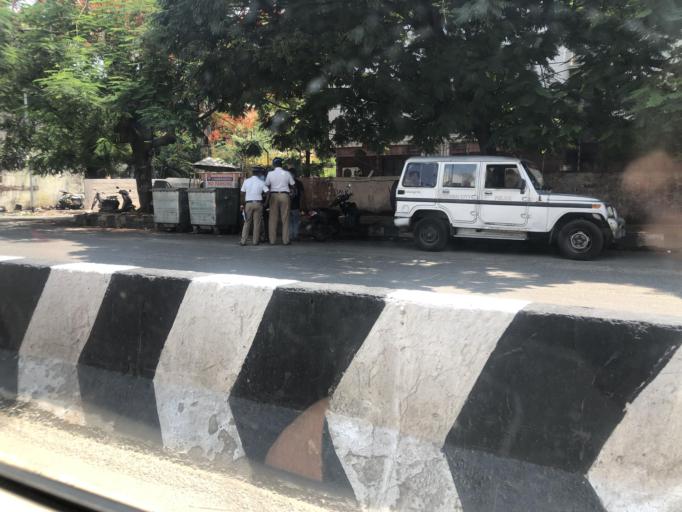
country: IN
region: Tamil Nadu
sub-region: Chennai
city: Gandhi Nagar
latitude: 12.9838
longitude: 80.2595
